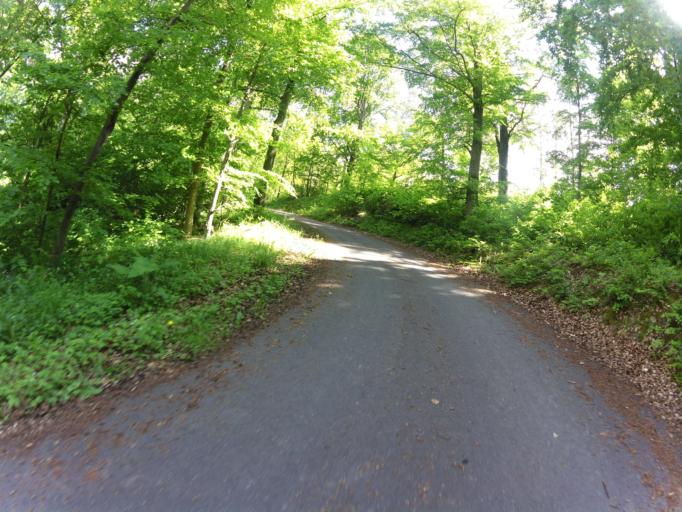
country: DE
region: Thuringia
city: Ifta
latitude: 51.0656
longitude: 10.1996
